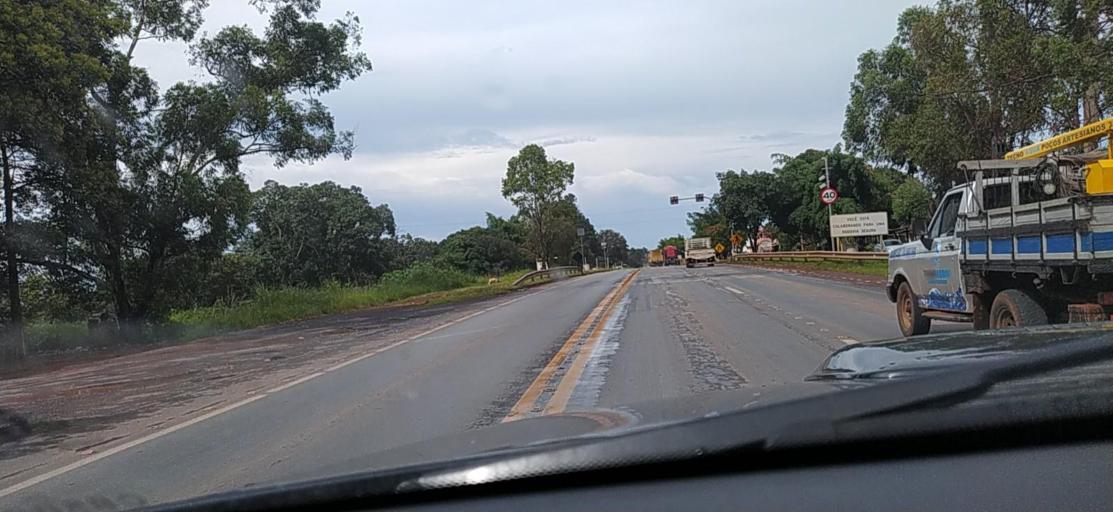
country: BR
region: Minas Gerais
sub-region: Montes Claros
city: Montes Claros
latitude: -16.8794
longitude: -43.8631
